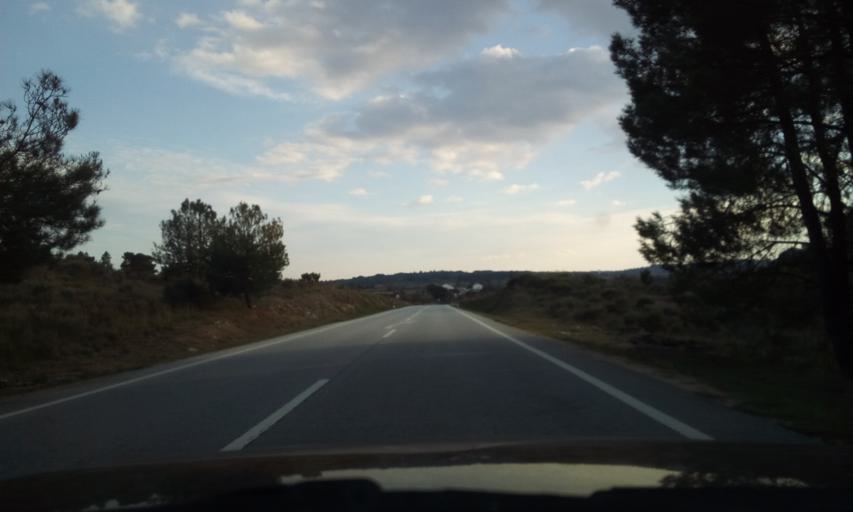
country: PT
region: Guarda
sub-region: Pinhel
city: Pinhel
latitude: 40.6784
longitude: -6.9503
